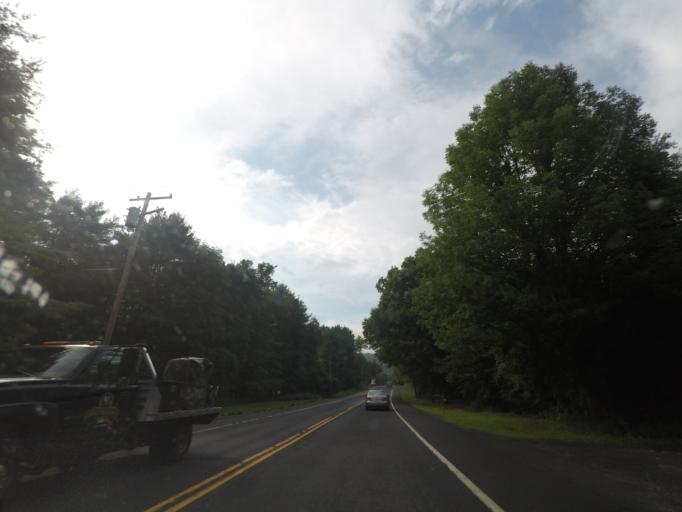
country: US
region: New York
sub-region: Rensselaer County
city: Nassau
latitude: 42.5007
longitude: -73.5570
